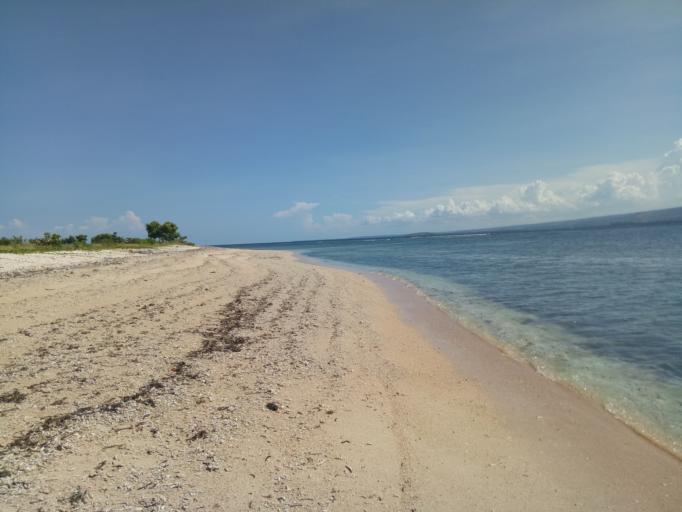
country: ID
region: West Nusa Tenggara
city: Sambelia
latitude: -8.4446
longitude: 116.7312
